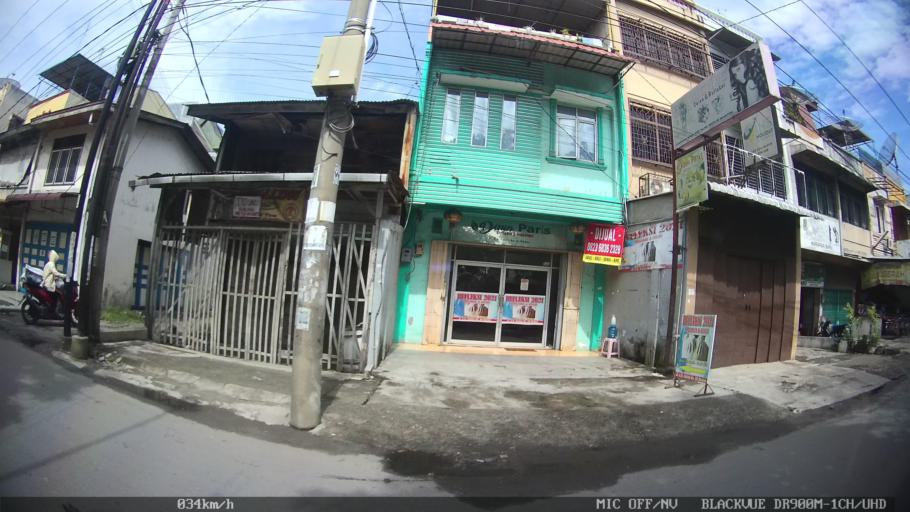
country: ID
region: North Sumatra
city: Medan
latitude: 3.5882
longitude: 98.7054
